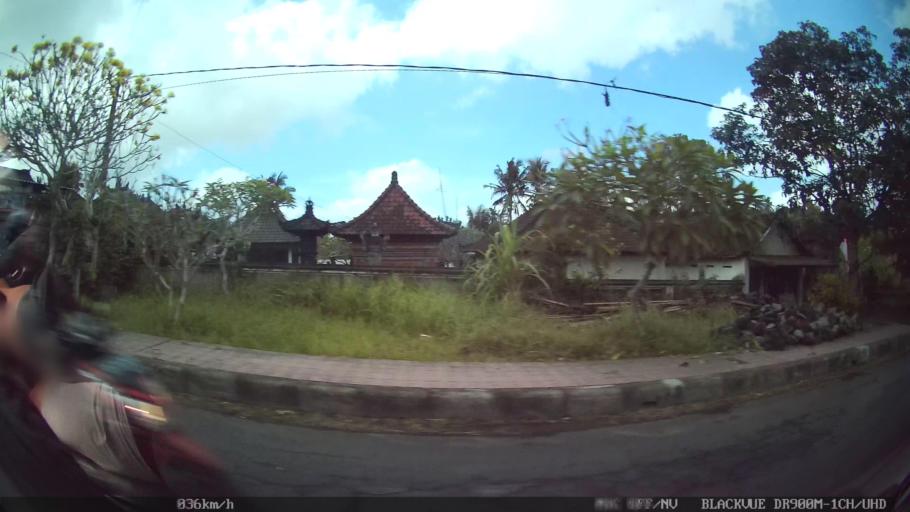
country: ID
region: Bali
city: Banjar Desa
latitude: -8.5834
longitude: 115.2704
